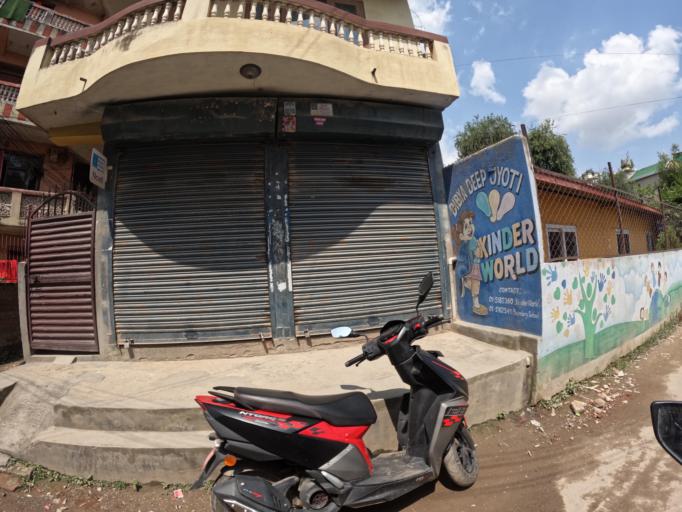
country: NP
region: Central Region
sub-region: Bagmati Zone
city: Patan
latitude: 27.6722
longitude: 85.3594
